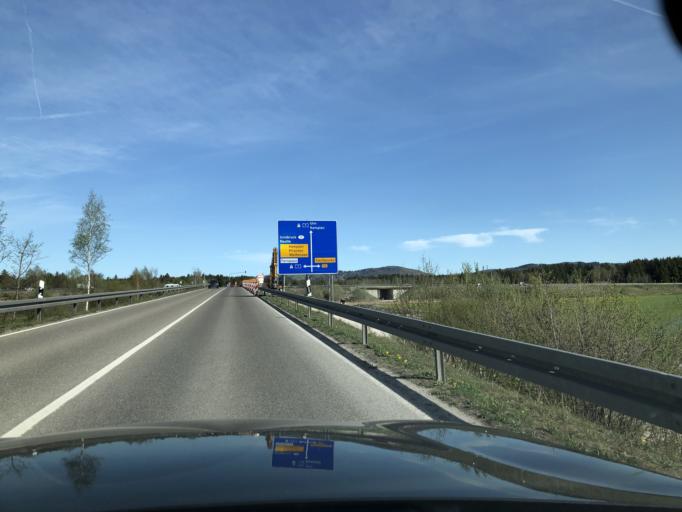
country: DE
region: Bavaria
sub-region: Swabia
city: Fuessen
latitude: 47.5721
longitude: 10.6645
